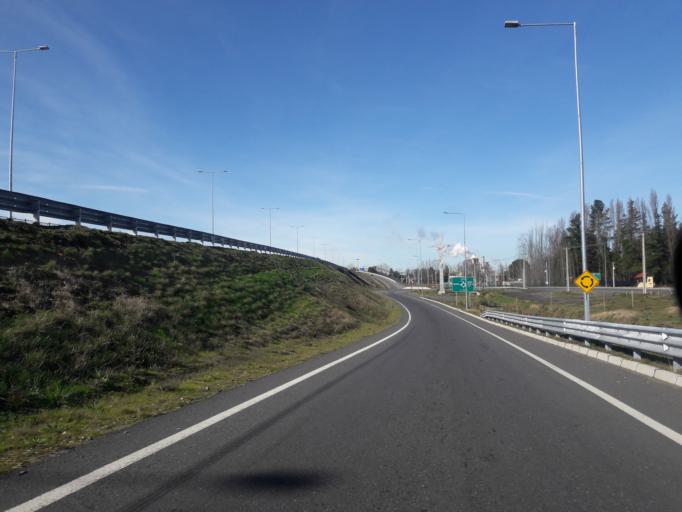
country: CL
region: Biobio
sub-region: Provincia de Biobio
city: Cabrero
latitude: -37.0387
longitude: -72.4073
